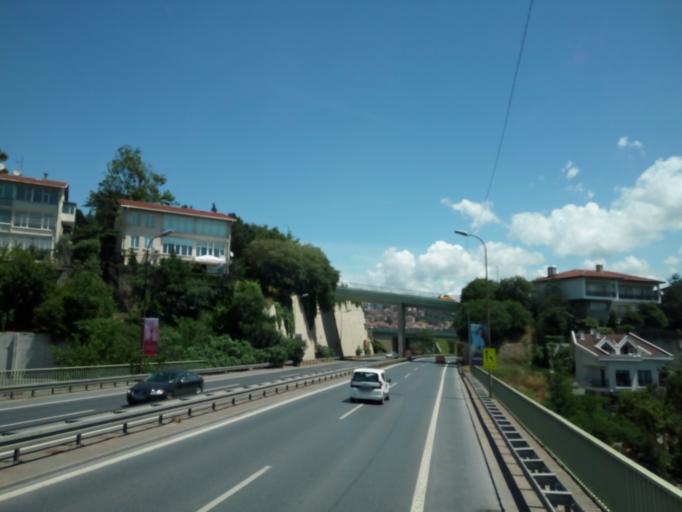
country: TR
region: Istanbul
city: Sisli
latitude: 41.0567
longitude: 29.0161
